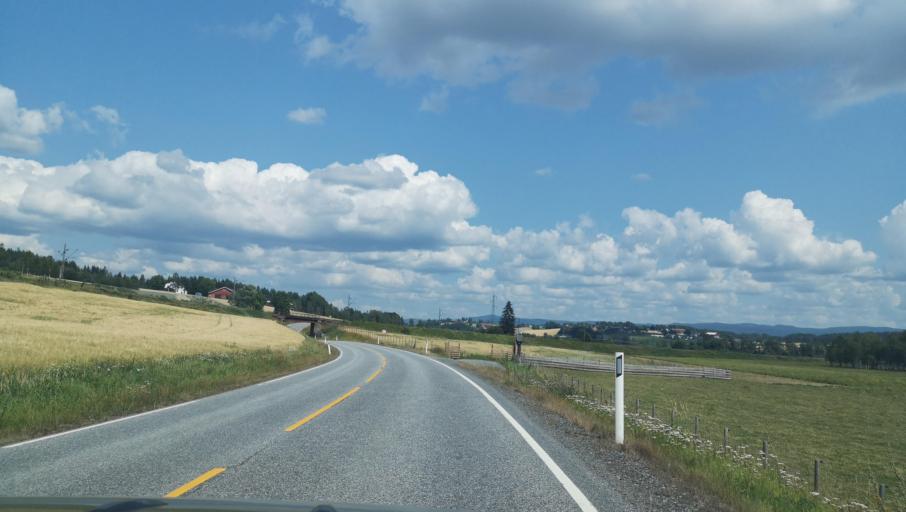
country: NO
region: Buskerud
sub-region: Ovre Eiker
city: Hokksund
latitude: 59.7145
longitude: 9.8212
